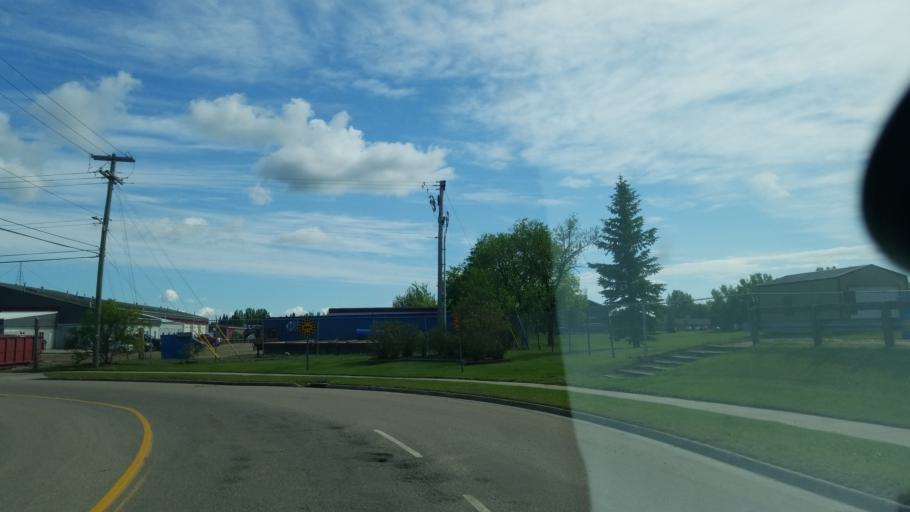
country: CA
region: Saskatchewan
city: Lloydminster
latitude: 53.2755
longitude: -110.0099
